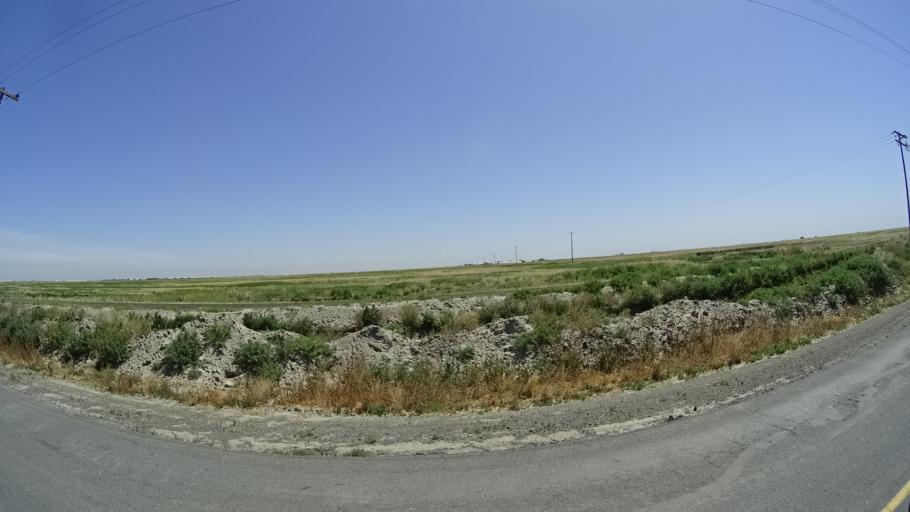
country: US
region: California
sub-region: Kings County
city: Stratford
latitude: 36.1680
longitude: -119.7174
